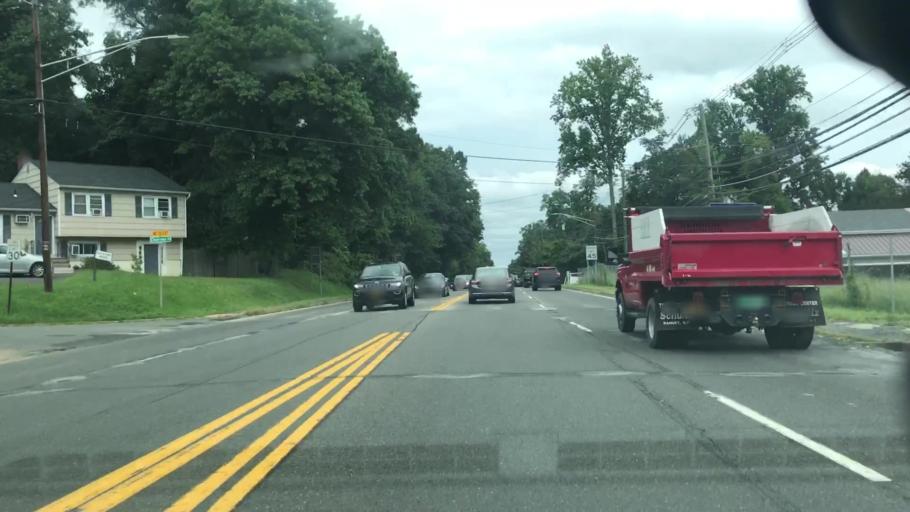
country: US
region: New York
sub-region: Rockland County
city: Bardonia
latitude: 41.1222
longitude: -73.9927
